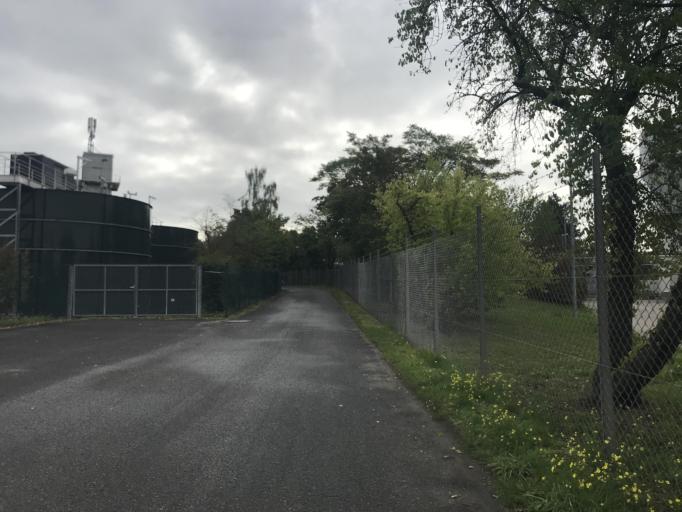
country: DE
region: Rheinland-Pfalz
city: Ingelheim am Rhein
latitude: 49.9812
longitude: 8.0456
